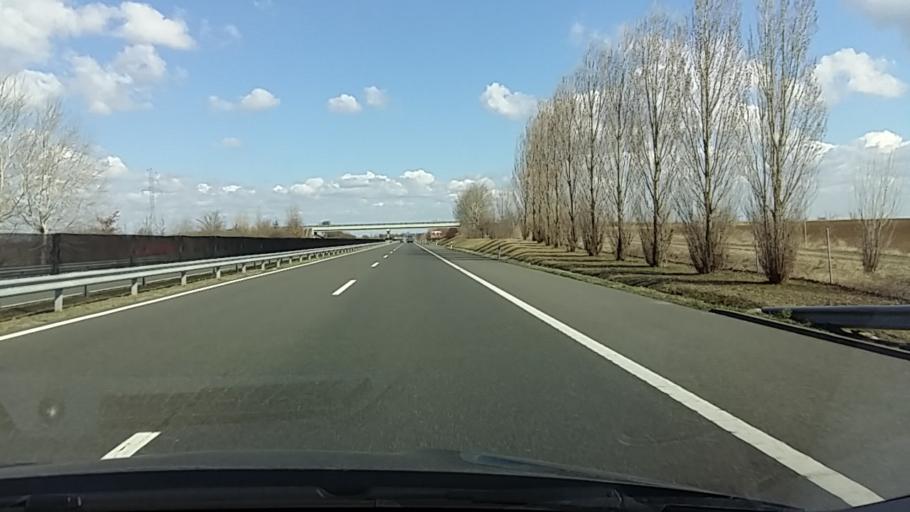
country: HU
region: Baranya
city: Boly
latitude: 45.9791
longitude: 18.5449
